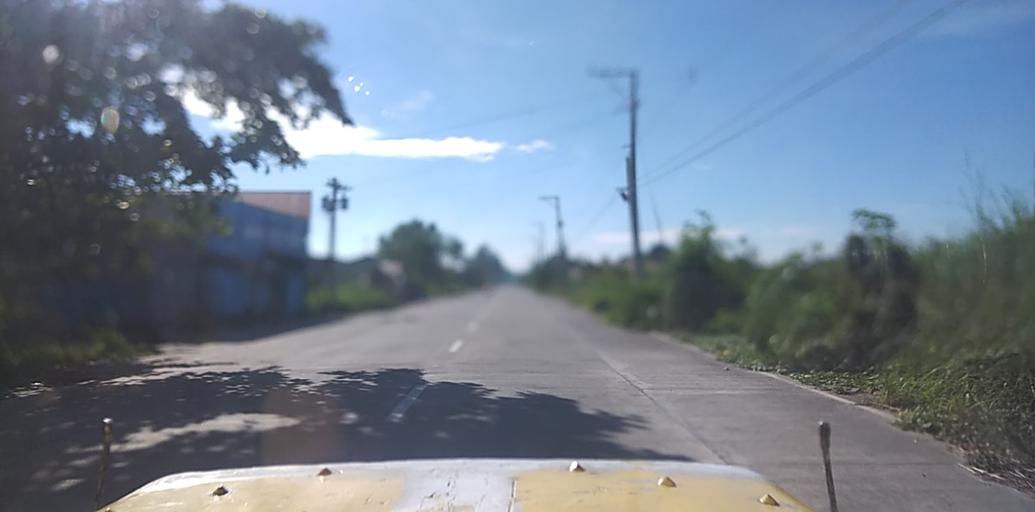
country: PH
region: Central Luzon
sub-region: Province of Pampanga
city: Anao
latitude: 15.1278
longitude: 120.6984
